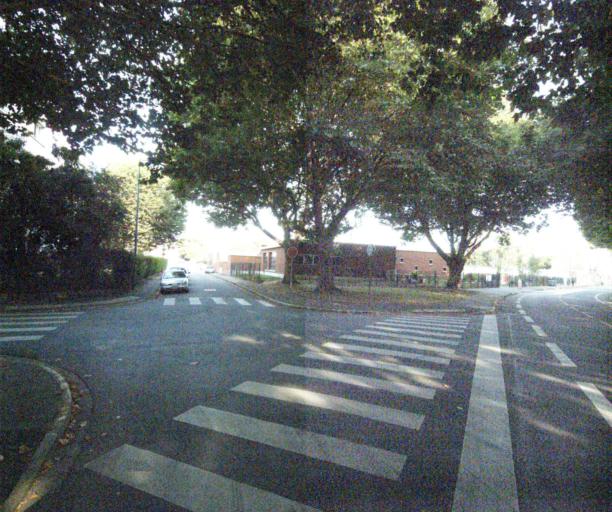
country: FR
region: Nord-Pas-de-Calais
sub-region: Departement du Nord
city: La Madeleine
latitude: 50.6291
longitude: 3.0852
